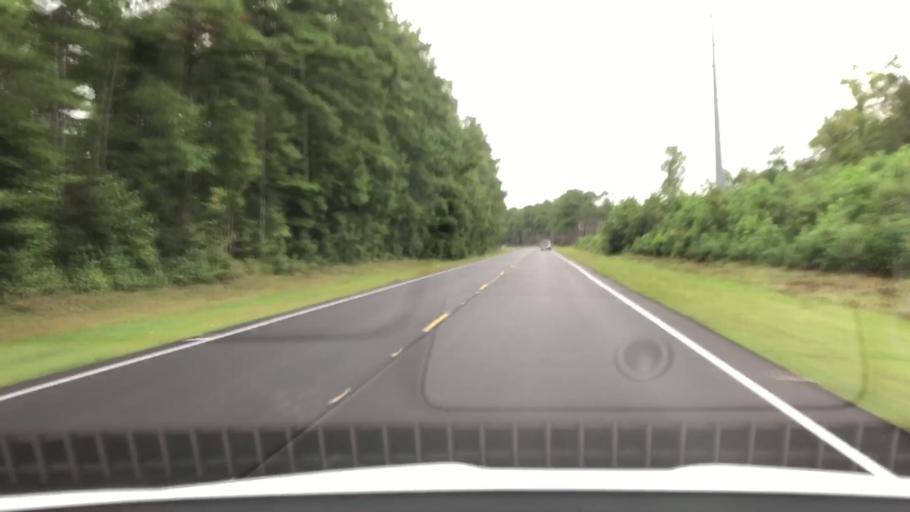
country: US
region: North Carolina
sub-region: Onslow County
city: Swansboro
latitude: 34.7686
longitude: -77.0968
